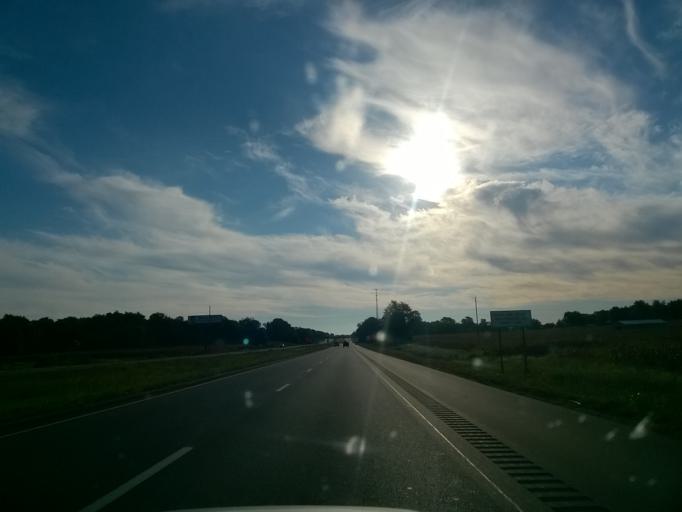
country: US
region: Indiana
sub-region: Gibson County
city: Haubstadt
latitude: 38.1696
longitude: -87.4530
